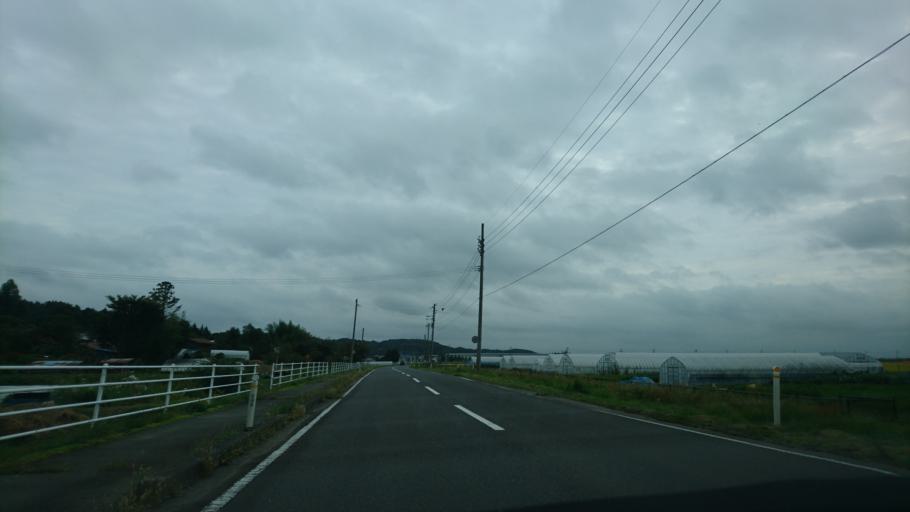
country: JP
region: Iwate
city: Ichinoseki
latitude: 38.8019
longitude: 141.1172
